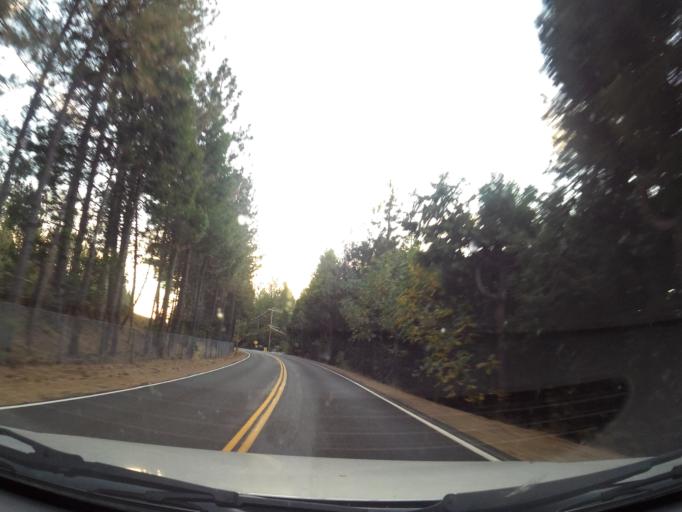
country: US
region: California
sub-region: El Dorado County
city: Camino
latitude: 38.7435
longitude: -120.6604
